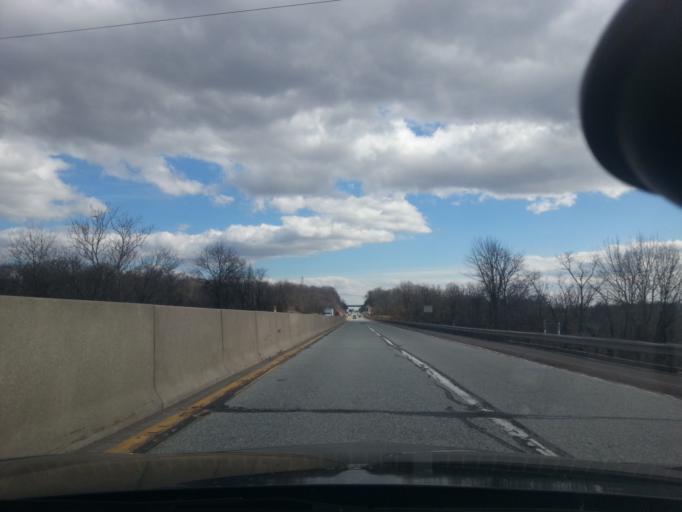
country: US
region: Pennsylvania
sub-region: Bucks County
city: Spinnerstown
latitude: 40.4714
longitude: -75.4537
